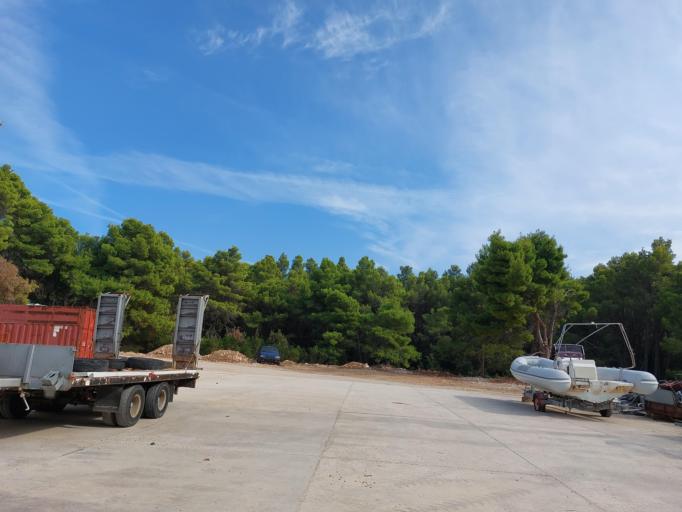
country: HR
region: Dubrovacko-Neretvanska
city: Smokvica
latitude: 42.7371
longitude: 16.8312
